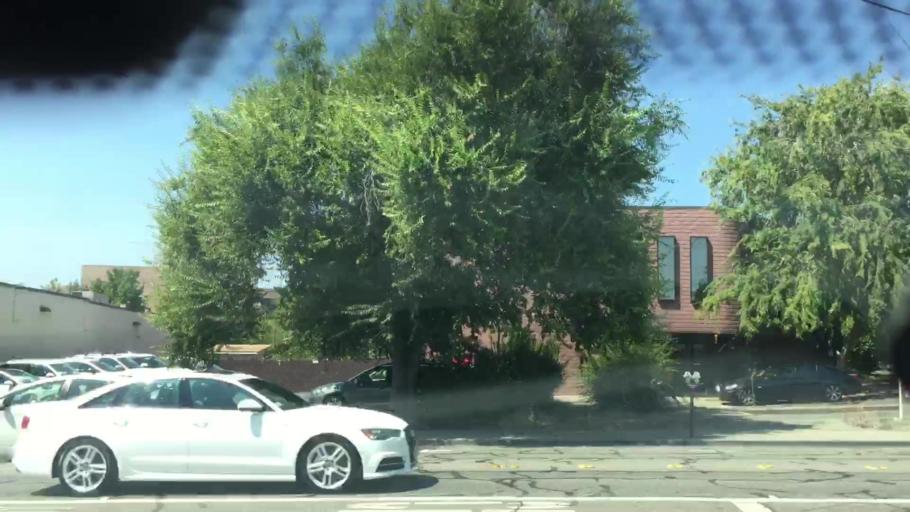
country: US
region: California
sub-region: Contra Costa County
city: Walnut Creek
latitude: 37.9079
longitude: -122.0616
